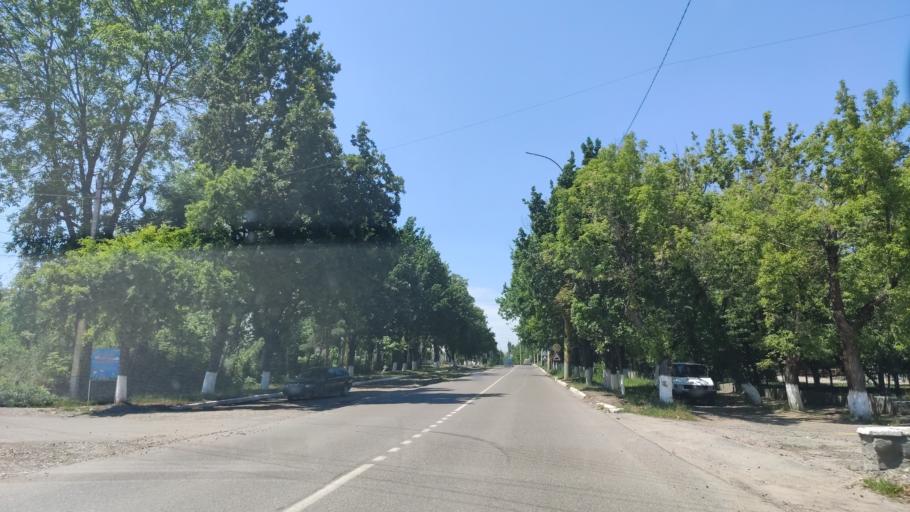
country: MD
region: Raionul Soroca
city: Soroca
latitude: 48.1620
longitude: 28.2856
